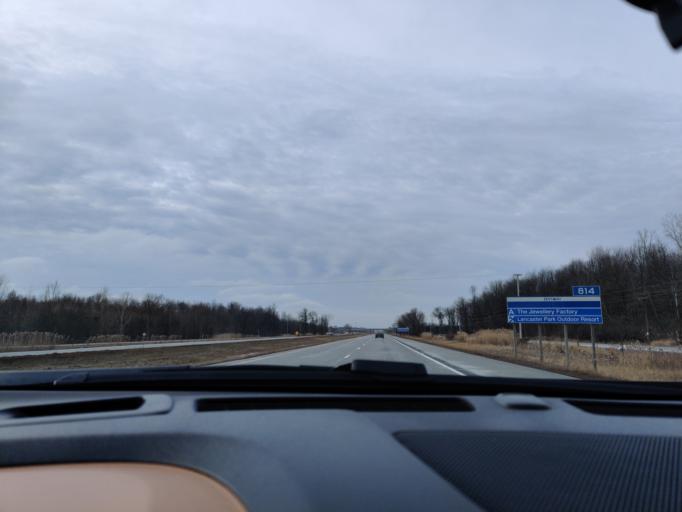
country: CA
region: Quebec
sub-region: Monteregie
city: Les Coteaux
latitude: 45.1668
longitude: -74.4340
